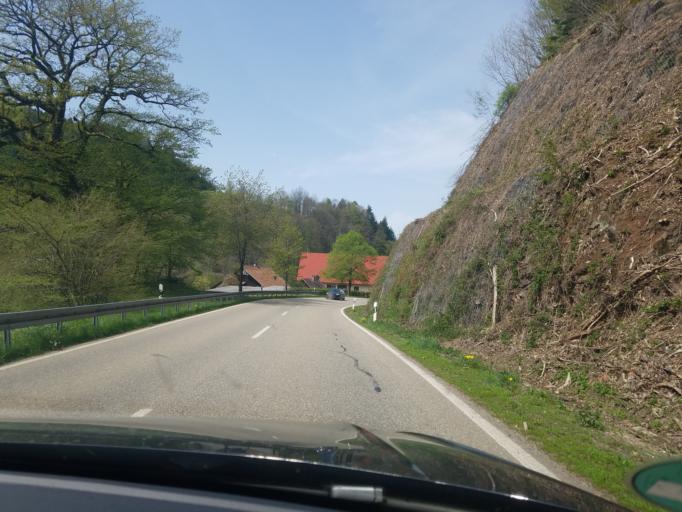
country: DE
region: Baden-Wuerttemberg
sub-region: Freiburg Region
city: Oppenau
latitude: 48.4394
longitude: 8.1718
